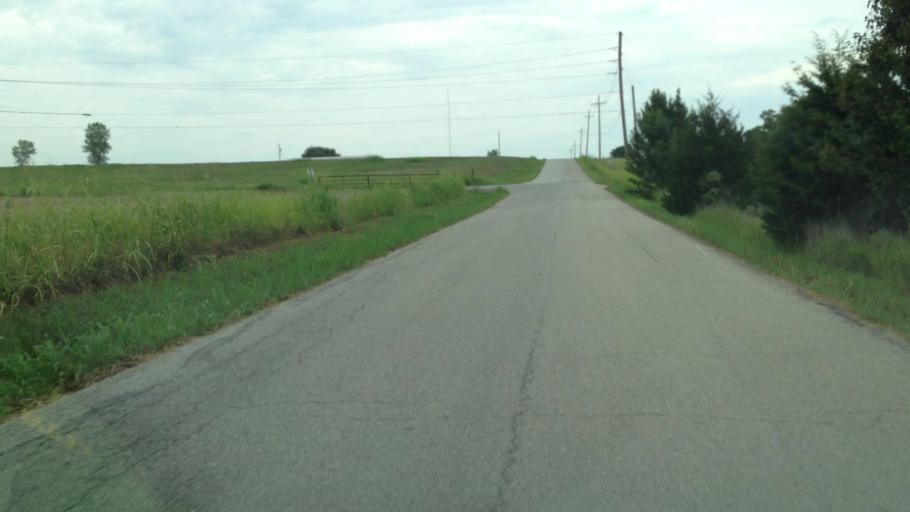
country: US
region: Oklahoma
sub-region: Craig County
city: Vinita
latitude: 36.6407
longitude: -95.1256
